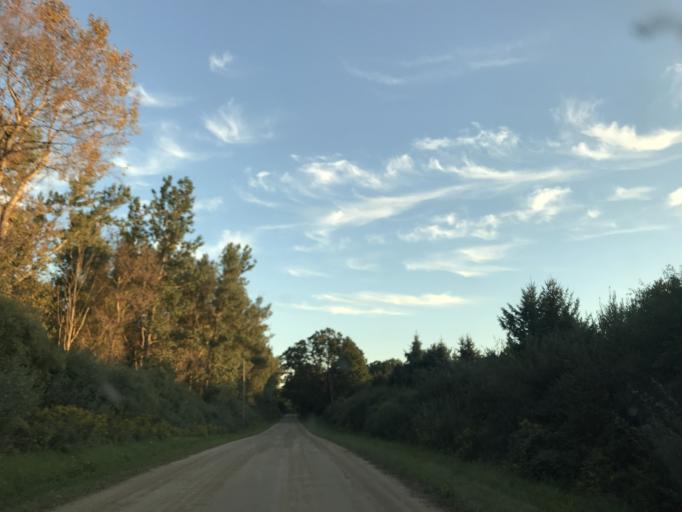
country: US
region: Michigan
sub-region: Mason County
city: Scottville
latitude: 43.9247
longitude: -86.1689
